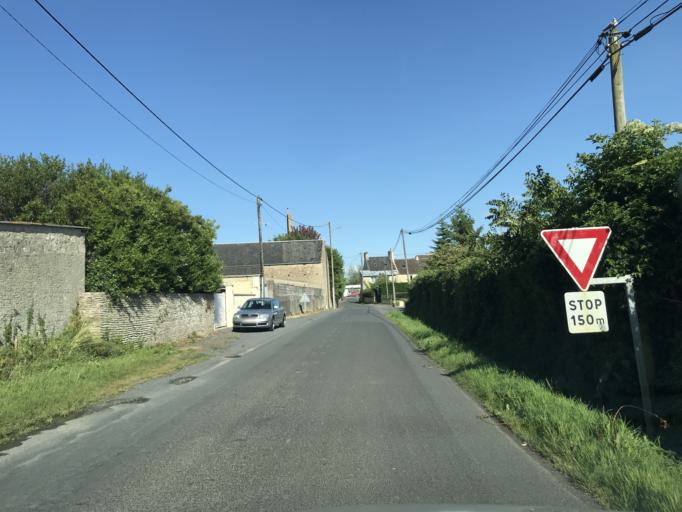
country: FR
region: Lower Normandy
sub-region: Departement du Calvados
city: Grandcamp-Maisy
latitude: 49.3817
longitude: -1.0587
